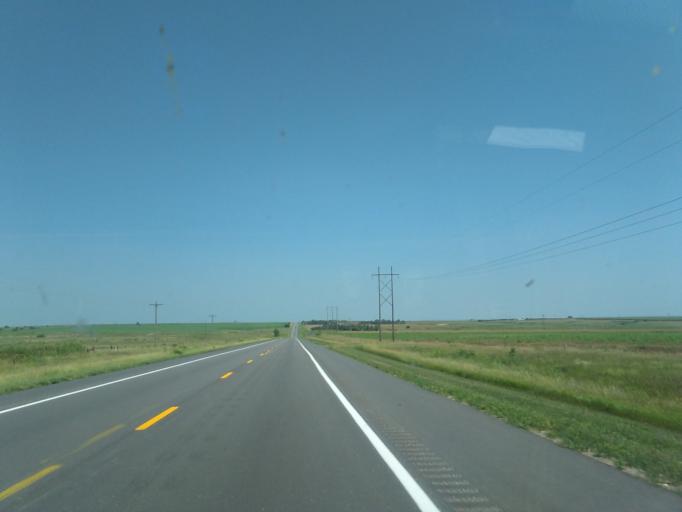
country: US
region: Nebraska
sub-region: Red Willow County
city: McCook
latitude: 40.2843
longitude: -100.6498
